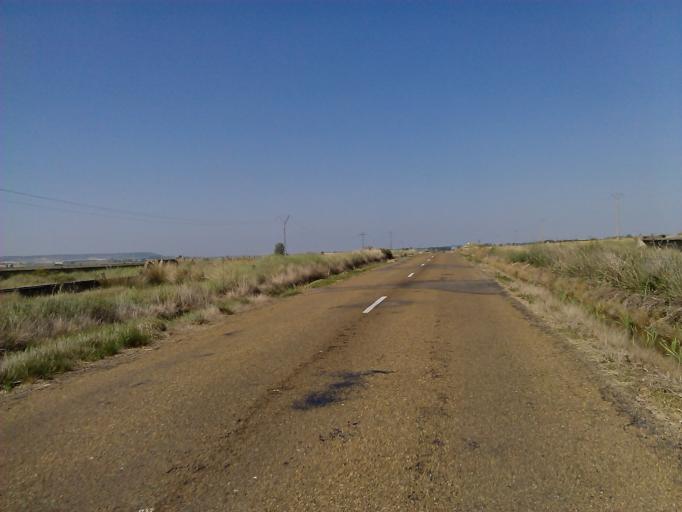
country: ES
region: Castille and Leon
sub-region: Provincia de Palencia
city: Boadilla del Camino
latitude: 42.2482
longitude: -4.3699
